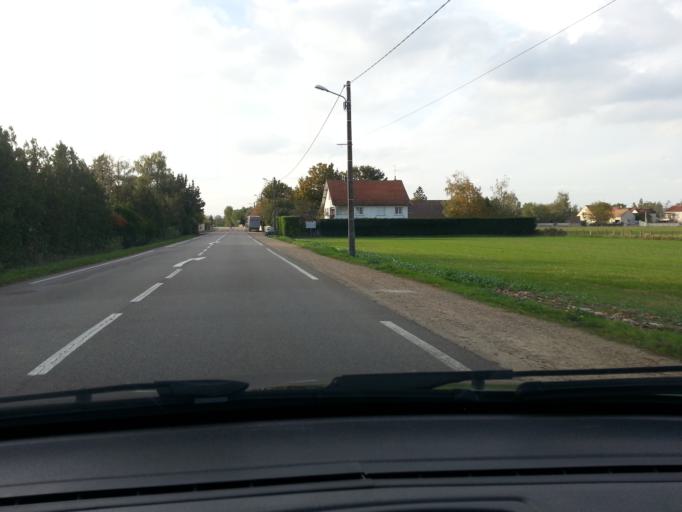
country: FR
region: Bourgogne
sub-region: Departement de Saone-et-Loire
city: Chatenoy-le-Royal
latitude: 46.7766
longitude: 4.8098
